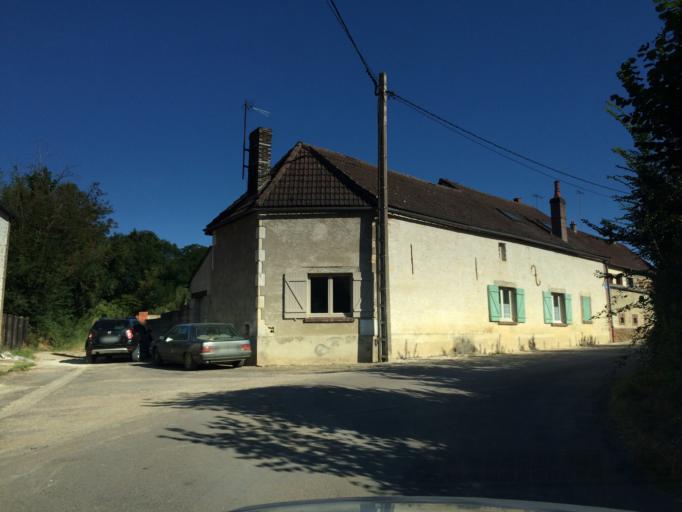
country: FR
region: Bourgogne
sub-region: Departement de l'Yonne
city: Fleury-la-Vallee
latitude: 47.9024
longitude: 3.4471
